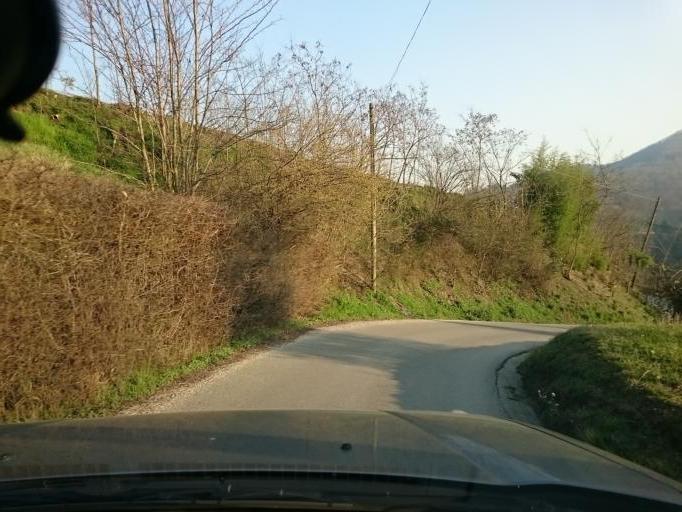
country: IT
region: Veneto
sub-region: Provincia di Padova
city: Torreglia
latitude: 45.3316
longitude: 11.7072
